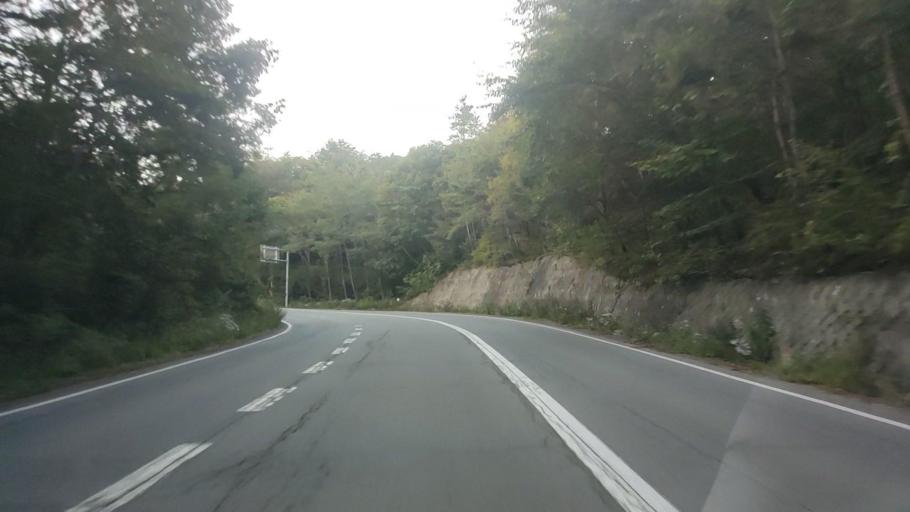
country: JP
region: Nagano
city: Komoro
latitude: 36.3905
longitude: 138.5843
